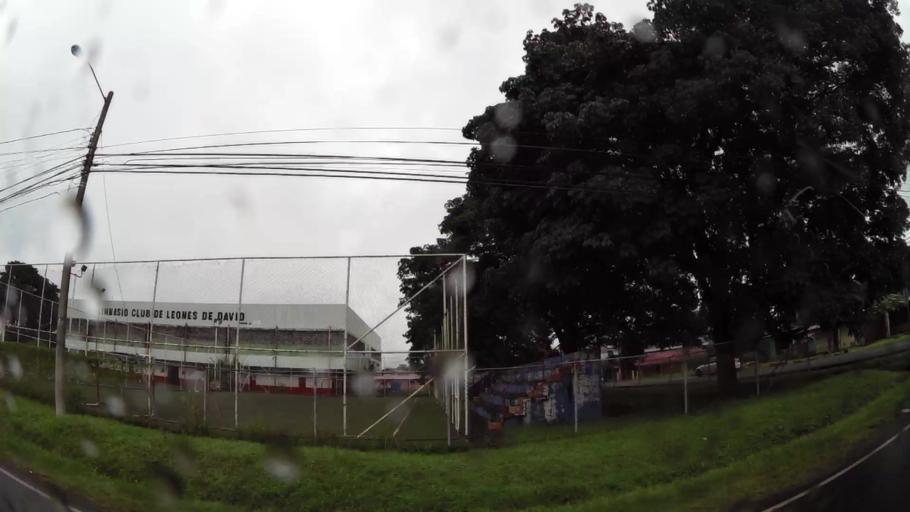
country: PA
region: Chiriqui
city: David
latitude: 8.4327
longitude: -82.4335
